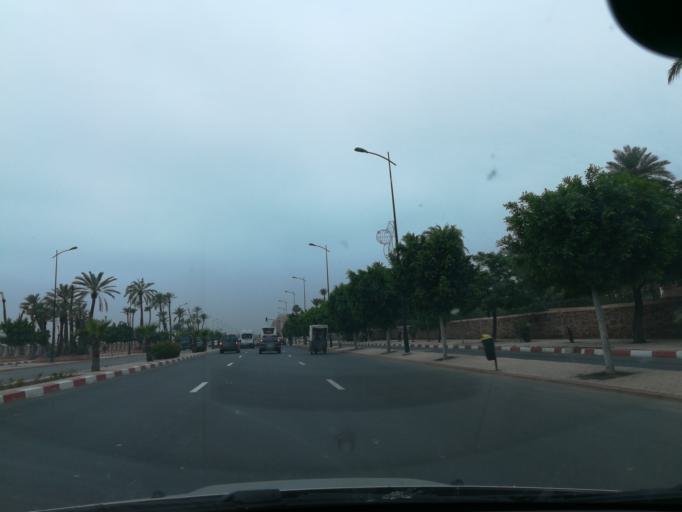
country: MA
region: Marrakech-Tensift-Al Haouz
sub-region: Marrakech
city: Marrakesh
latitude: 31.6430
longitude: -7.9951
